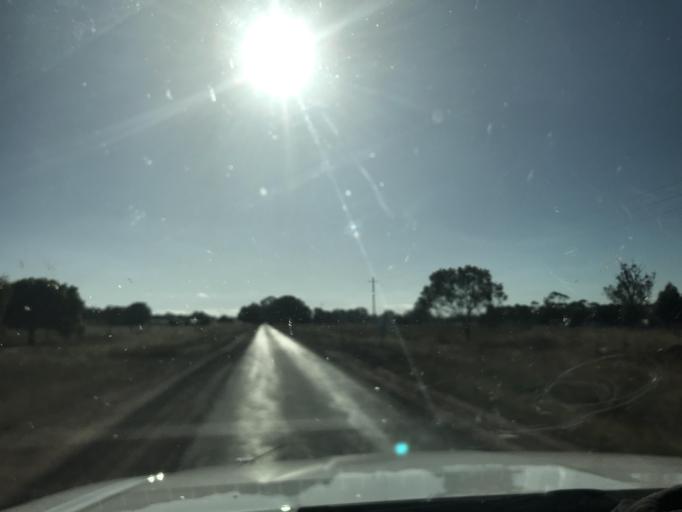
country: AU
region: Victoria
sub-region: Horsham
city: Horsham
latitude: -37.0036
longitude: 141.6058
